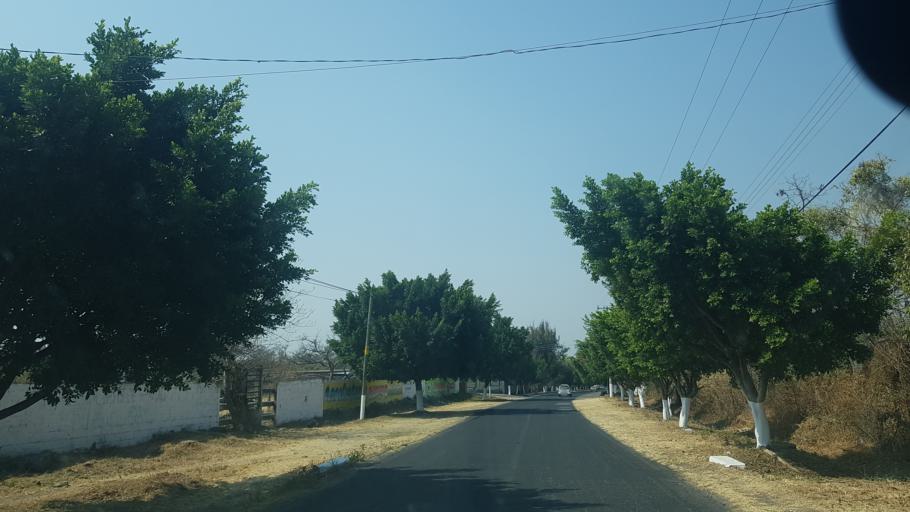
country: MX
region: Morelos
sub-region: Zacualpan
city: Zacualpan de Amilpas
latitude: 18.7984
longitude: -98.7641
